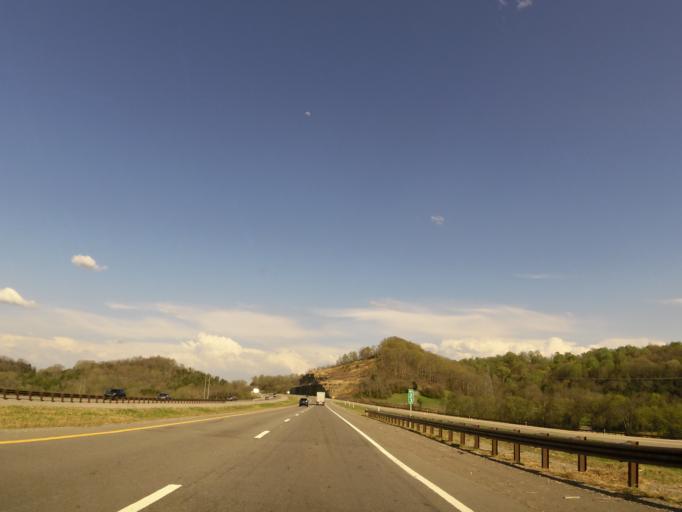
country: US
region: Tennessee
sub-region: Williamson County
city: Thompson's Station
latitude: 35.8153
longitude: -86.9816
